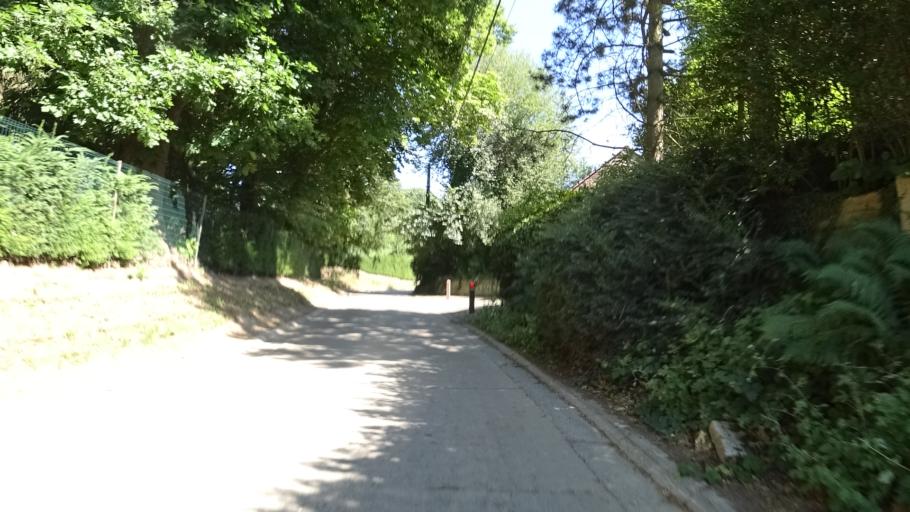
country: BE
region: Wallonia
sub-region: Province du Brabant Wallon
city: Jodoigne
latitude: 50.7051
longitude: 4.8459
